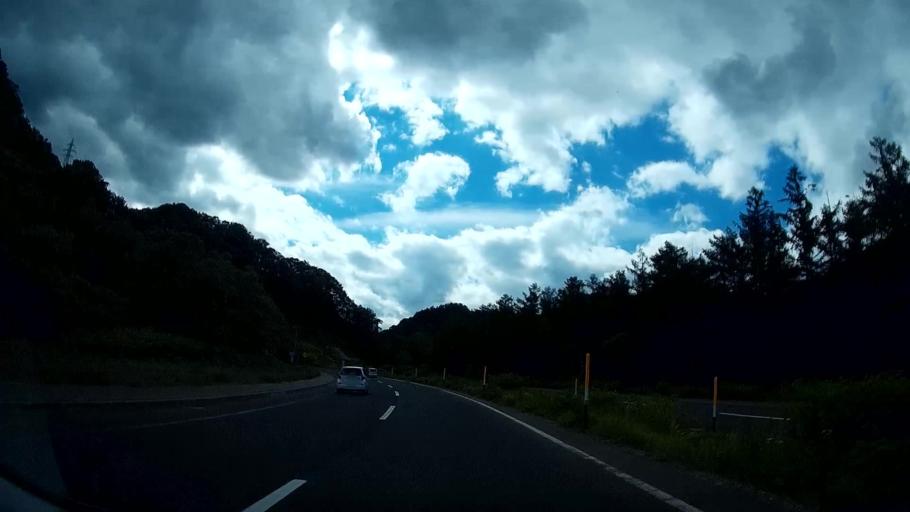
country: JP
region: Hokkaido
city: Sapporo
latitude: 42.9698
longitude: 141.1905
